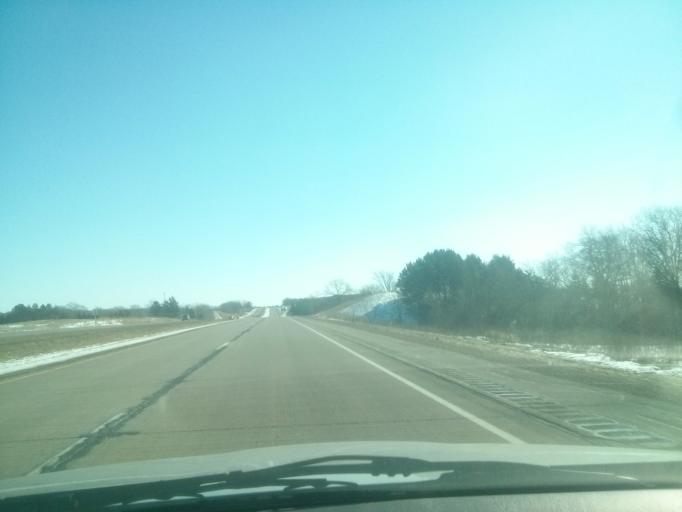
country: US
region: Wisconsin
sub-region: Saint Croix County
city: Somerset
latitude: 45.1227
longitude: -92.6170
